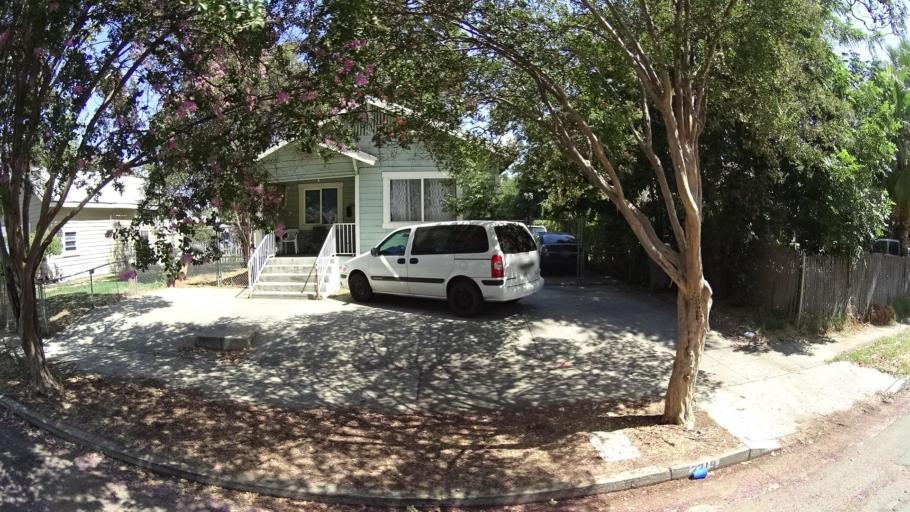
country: US
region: California
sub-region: Fresno County
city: Fresno
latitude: 36.7564
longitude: -119.7849
